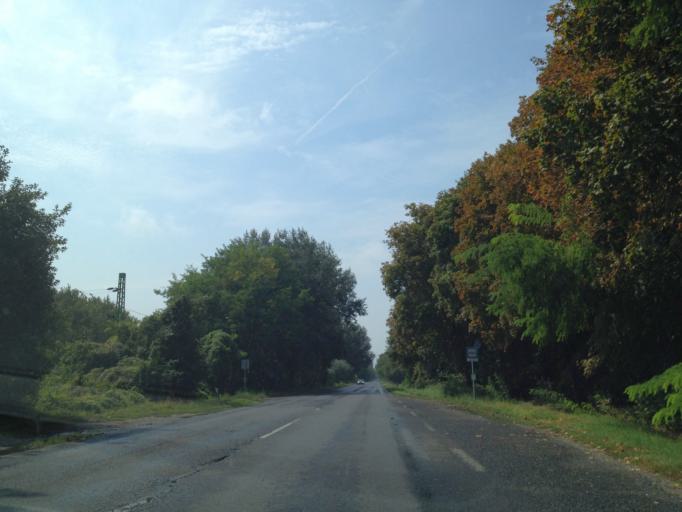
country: HU
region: Komarom-Esztergom
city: Acs
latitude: 47.7314
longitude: 18.0607
